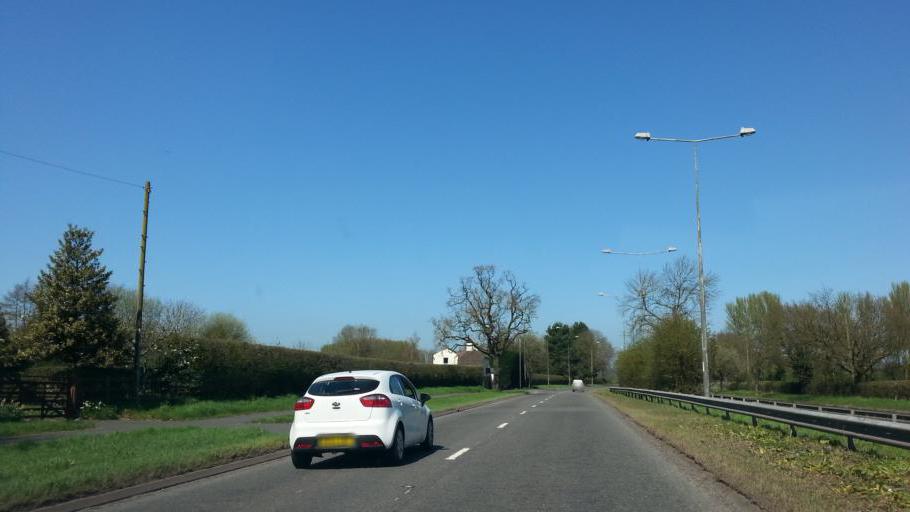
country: GB
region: England
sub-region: Staffordshire
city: Brewood
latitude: 52.6846
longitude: -2.1337
